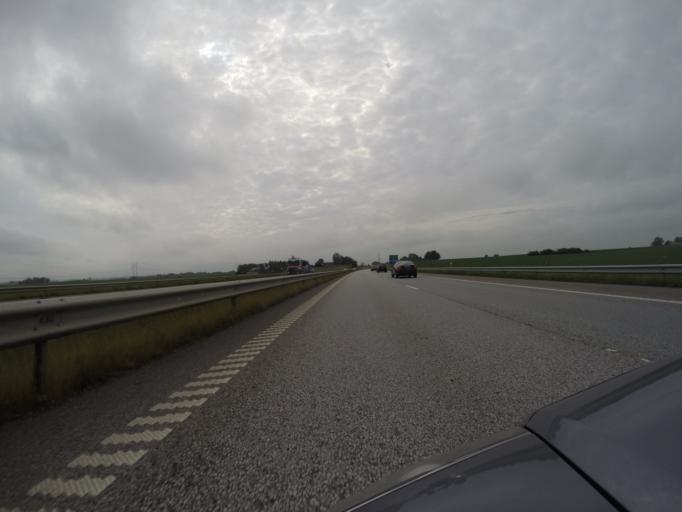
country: SE
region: Skane
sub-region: Lomma Kommun
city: Lomma
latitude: 55.7299
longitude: 13.0818
